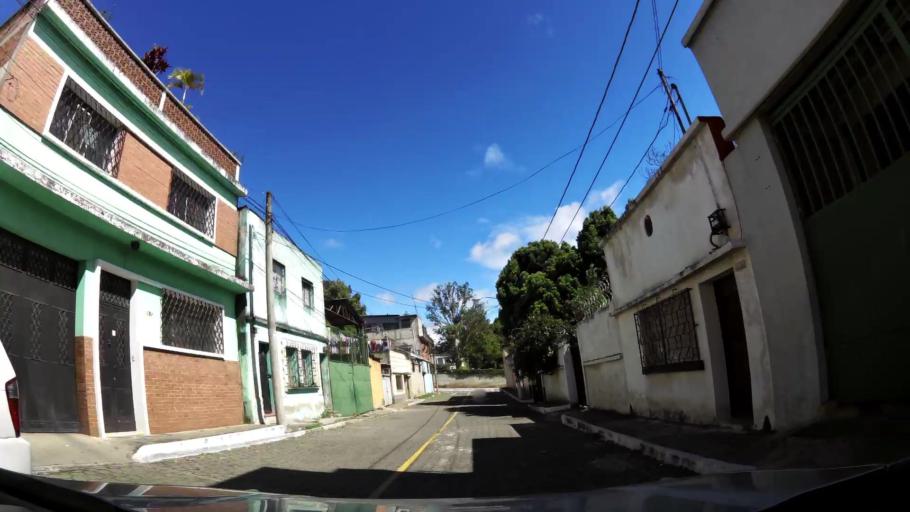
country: GT
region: Guatemala
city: Guatemala City
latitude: 14.6107
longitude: -90.5297
